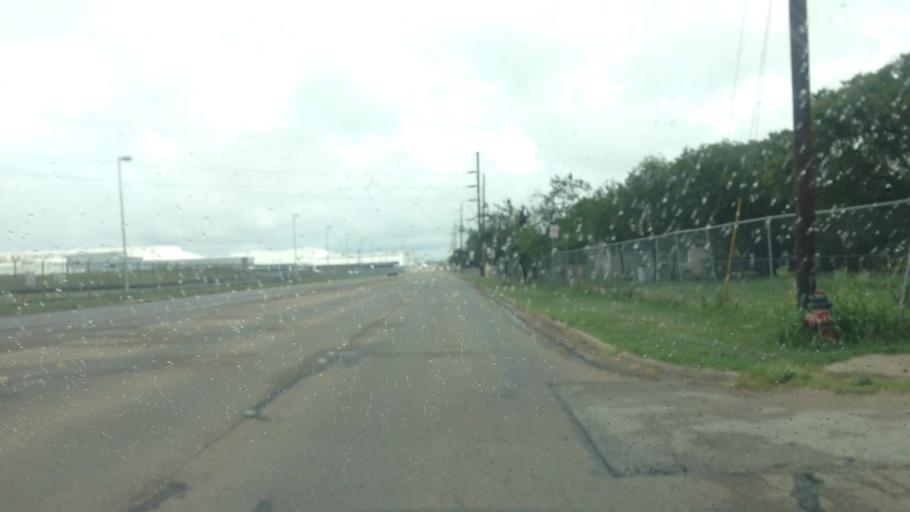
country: US
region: Texas
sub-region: Tarrant County
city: White Settlement
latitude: 32.7655
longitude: -97.4571
